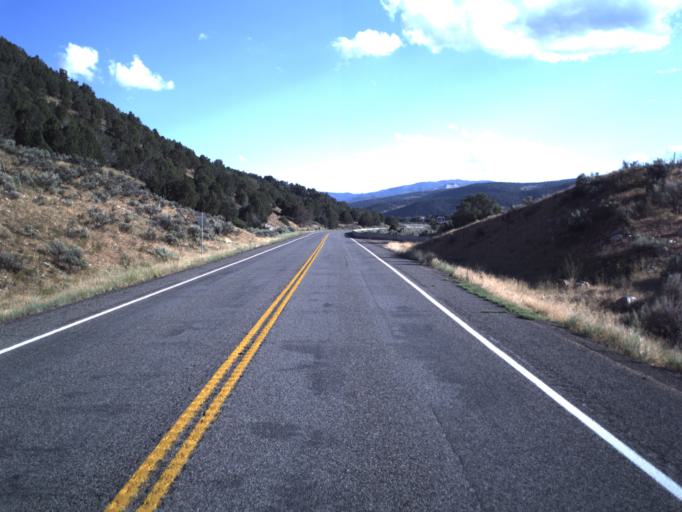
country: US
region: Utah
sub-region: Utah County
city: Woodland Hills
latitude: 39.9422
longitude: -111.5409
